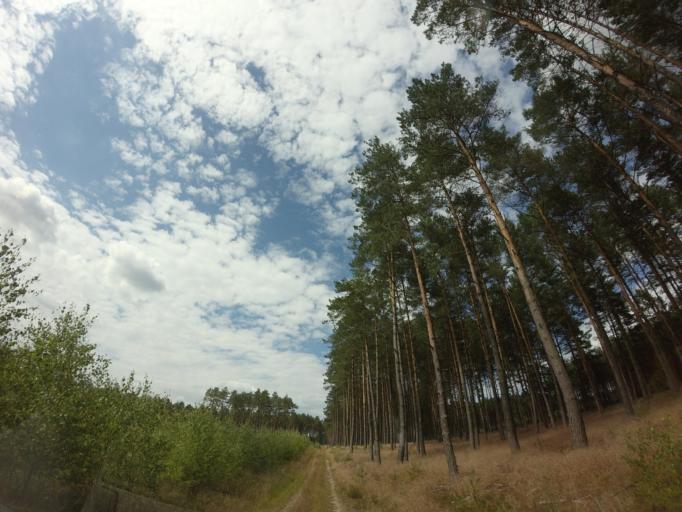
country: PL
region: West Pomeranian Voivodeship
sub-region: Powiat choszczenski
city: Drawno
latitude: 53.1568
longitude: 15.7376
